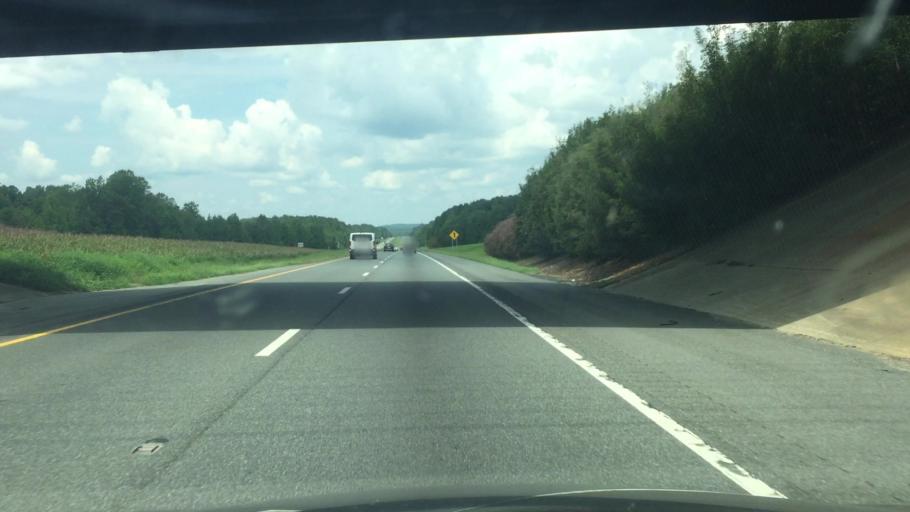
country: US
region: North Carolina
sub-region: Randolph County
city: Asheboro
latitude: 35.5360
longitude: -79.7905
